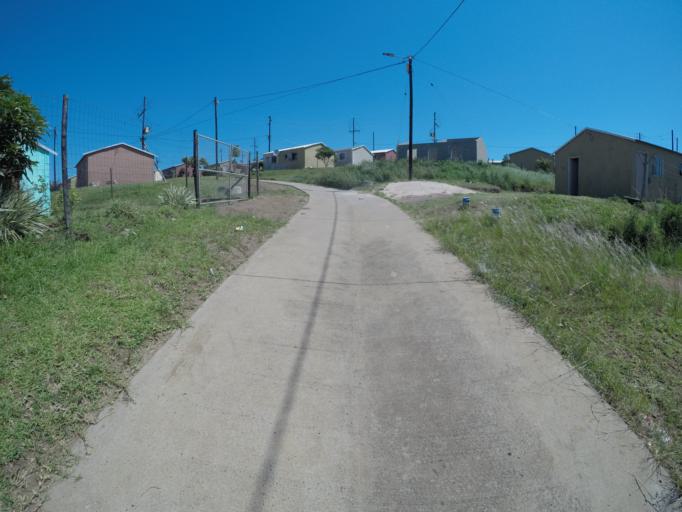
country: ZA
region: KwaZulu-Natal
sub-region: uThungulu District Municipality
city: Empangeni
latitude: -28.7621
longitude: 31.8771
